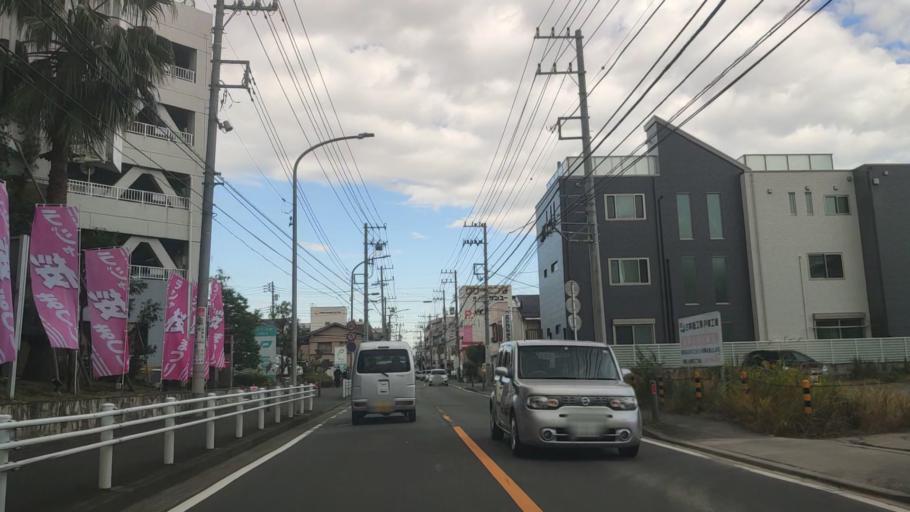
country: JP
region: Kanagawa
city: Fujisawa
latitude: 35.4204
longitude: 139.5356
